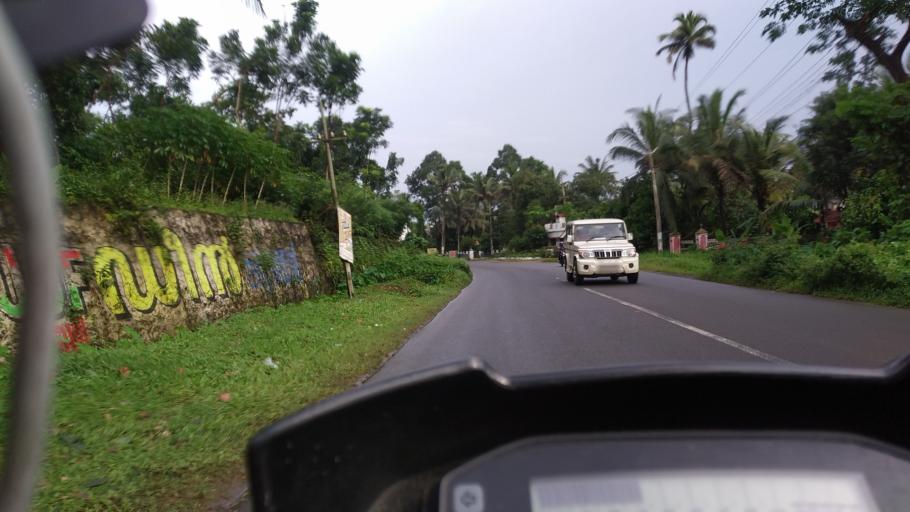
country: IN
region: Kerala
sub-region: Ernakulam
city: Kotamangalam
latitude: 10.0566
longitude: 76.6956
